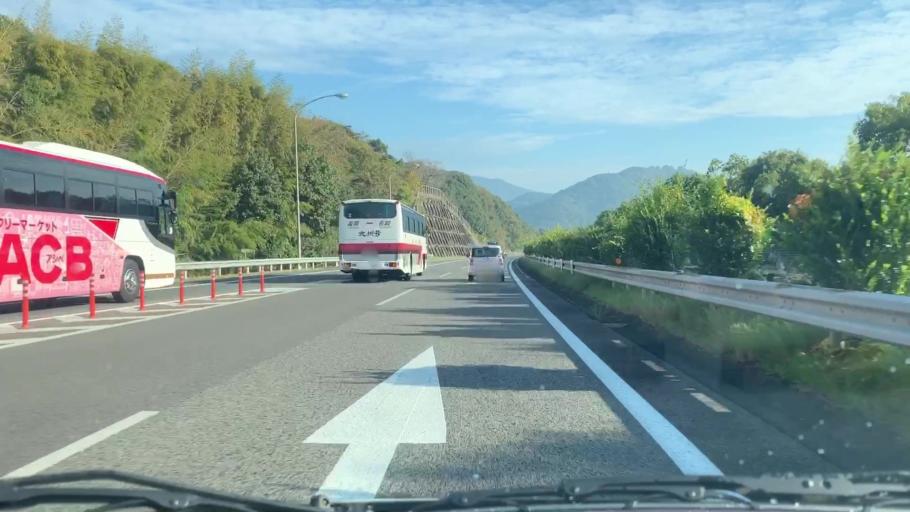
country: JP
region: Saga Prefecture
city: Takeocho-takeo
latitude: 33.2631
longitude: 130.0841
